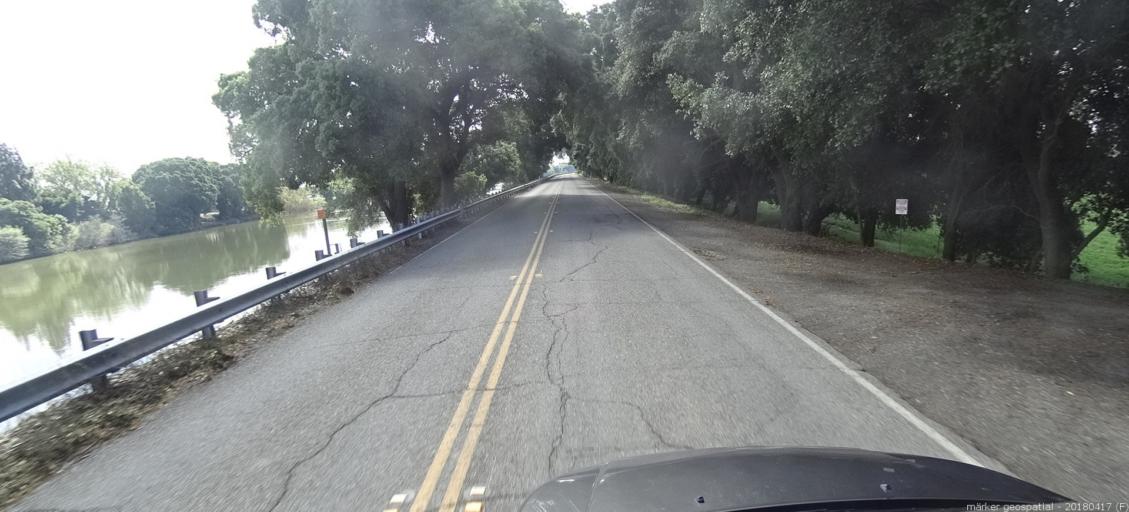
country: US
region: California
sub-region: Sacramento County
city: Walnut Grove
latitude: 38.2579
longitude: -121.5190
